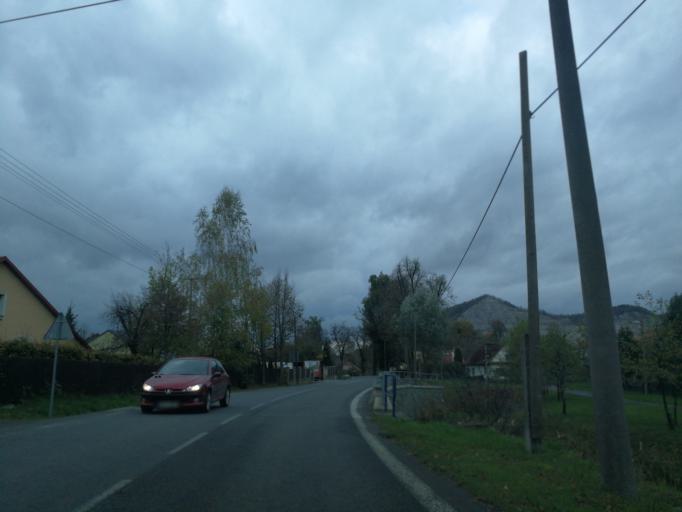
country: CZ
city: Stramberk
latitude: 49.5700
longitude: 18.1101
